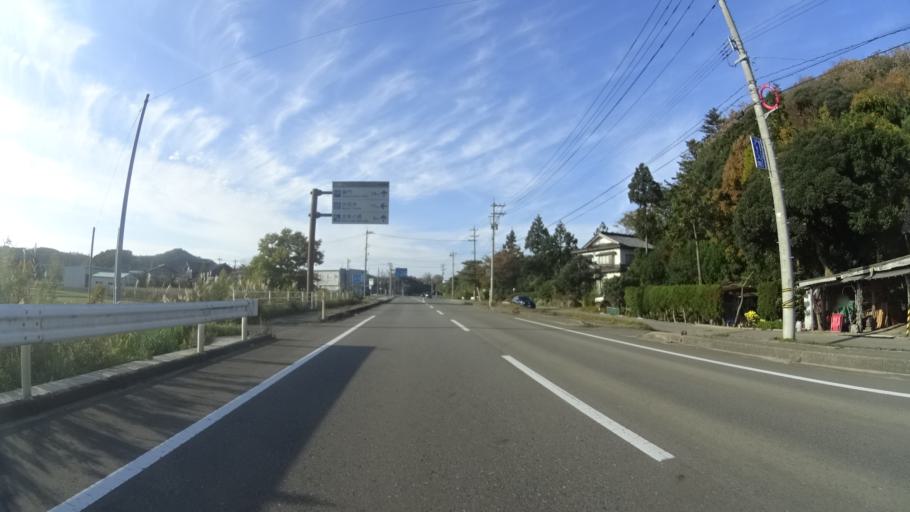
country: JP
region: Ishikawa
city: Hakui
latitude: 37.0213
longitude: 136.7882
